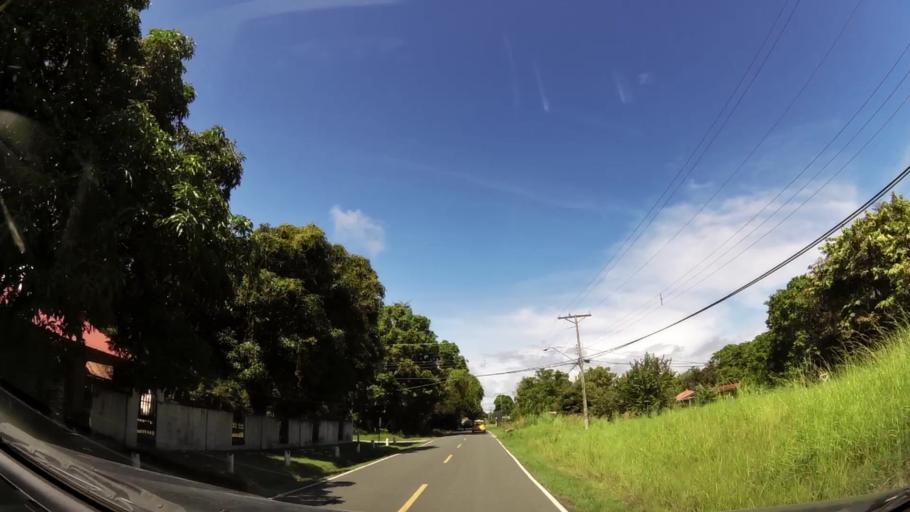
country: PA
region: Panama
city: Nueva Gorgona
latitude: 8.5499
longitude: -79.8751
